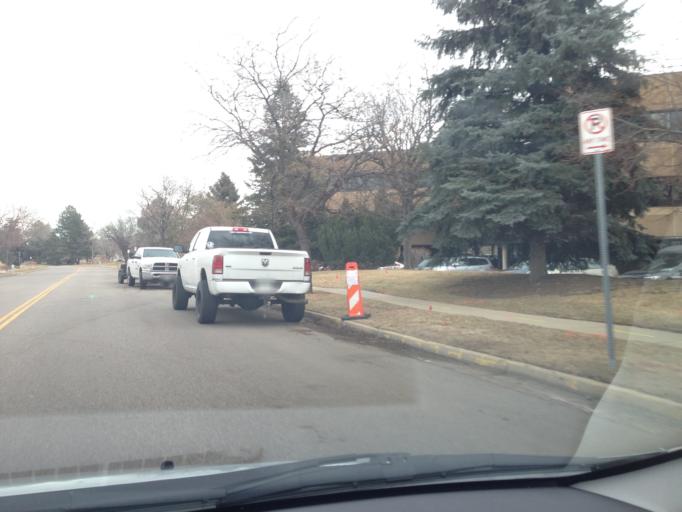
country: US
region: Colorado
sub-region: Boulder County
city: Boulder
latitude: 40.0156
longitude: -105.2456
